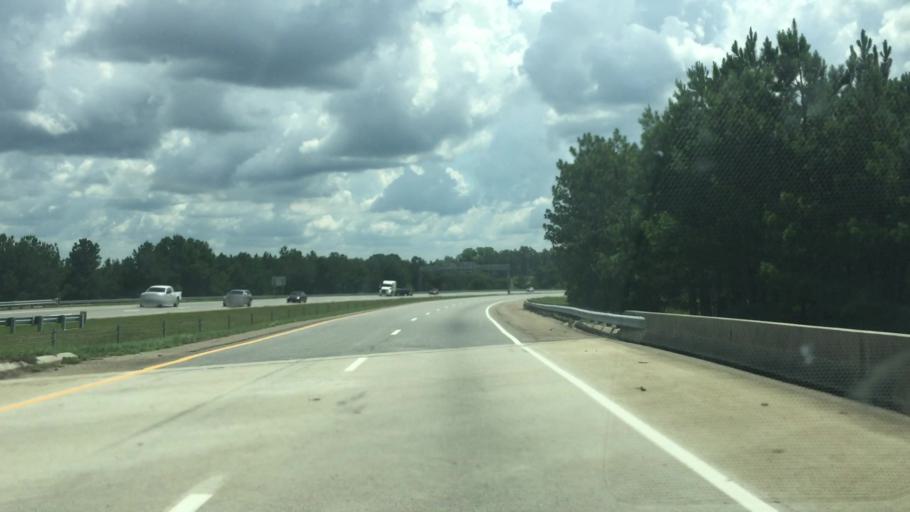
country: US
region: North Carolina
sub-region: Richmond County
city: Hamlet
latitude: 34.8686
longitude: -79.6489
